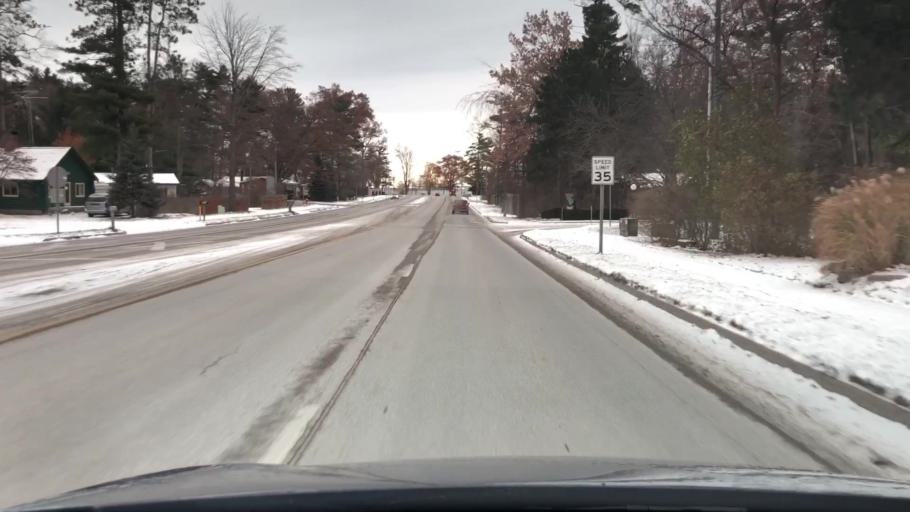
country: US
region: Michigan
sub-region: Grand Traverse County
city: Traverse City
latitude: 44.7463
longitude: -85.5601
